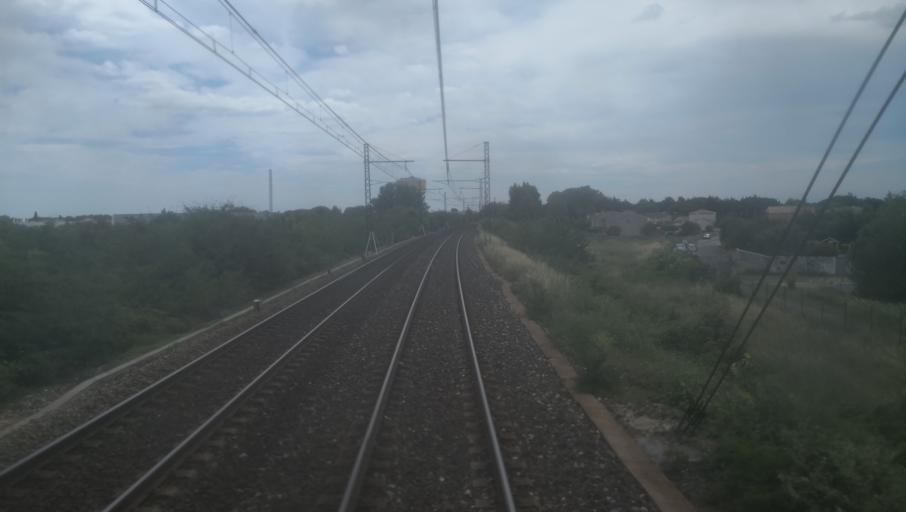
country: FR
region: Languedoc-Roussillon
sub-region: Departement de l'Herault
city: Lunel
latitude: 43.6874
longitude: 4.1469
